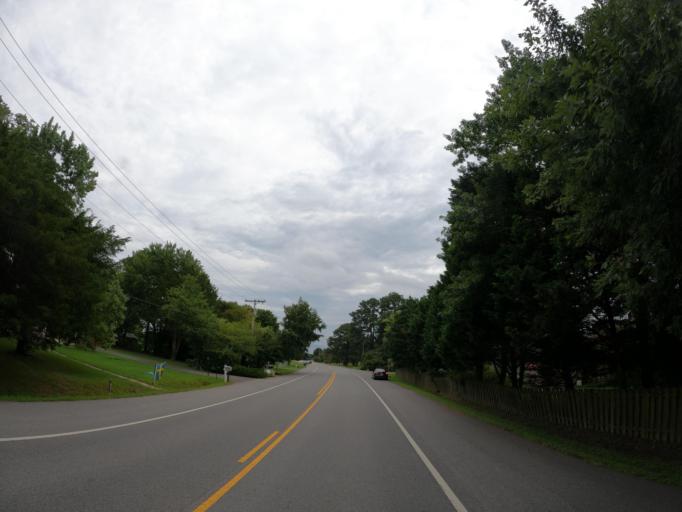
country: US
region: Maryland
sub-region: Saint Mary's County
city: Lexington Park
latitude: 38.1414
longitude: -76.5065
